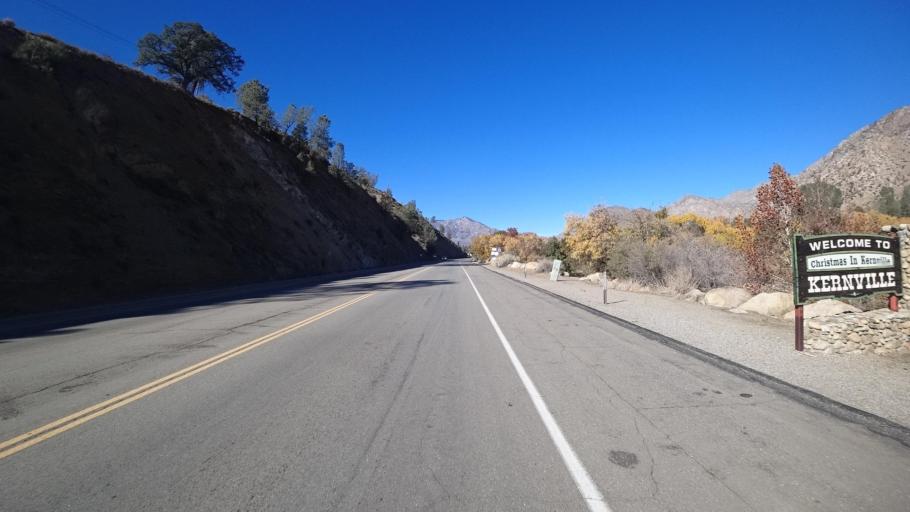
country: US
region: California
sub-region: Kern County
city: Kernville
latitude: 35.7506
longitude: -118.4234
